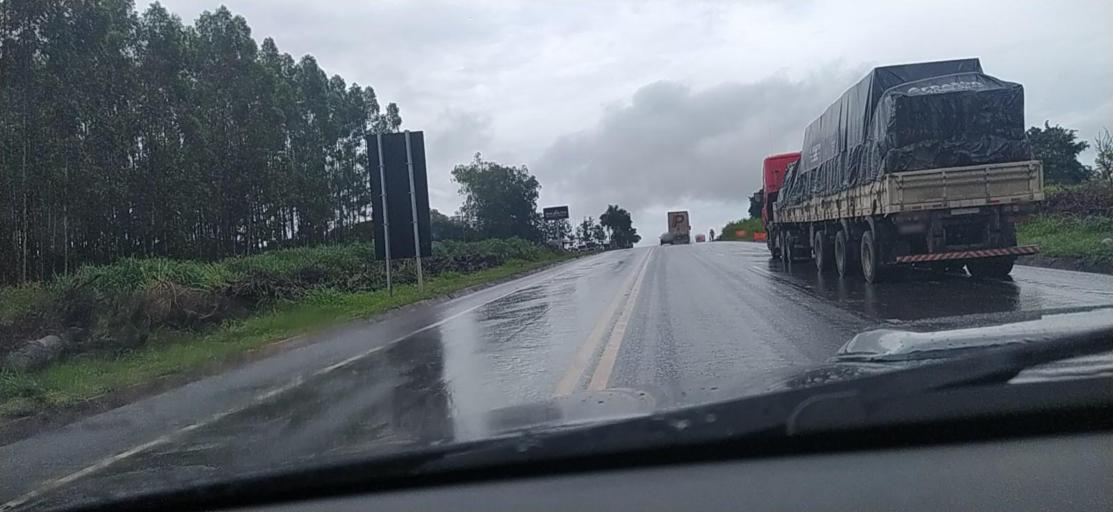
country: BR
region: Minas Gerais
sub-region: Curvelo
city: Curvelo
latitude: -18.9419
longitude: -44.4972
